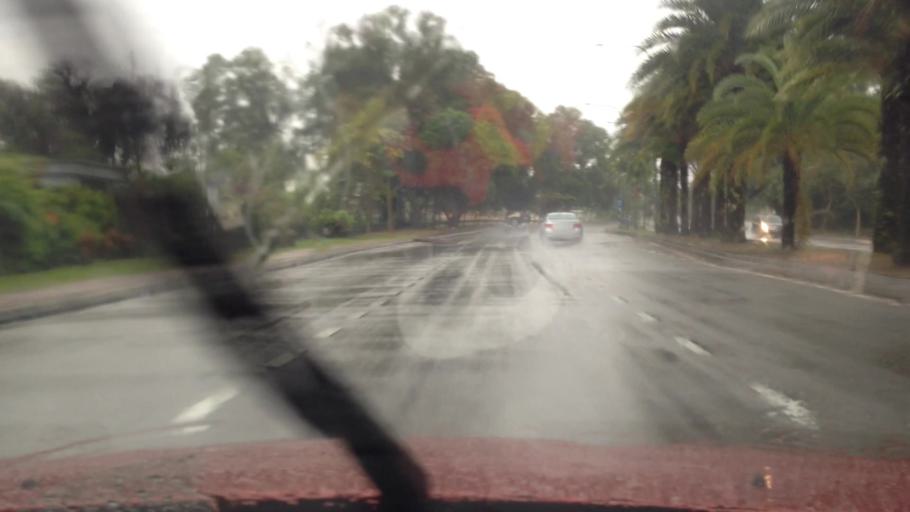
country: MY
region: Selangor
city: Subang Jaya
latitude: 3.0531
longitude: 101.5707
